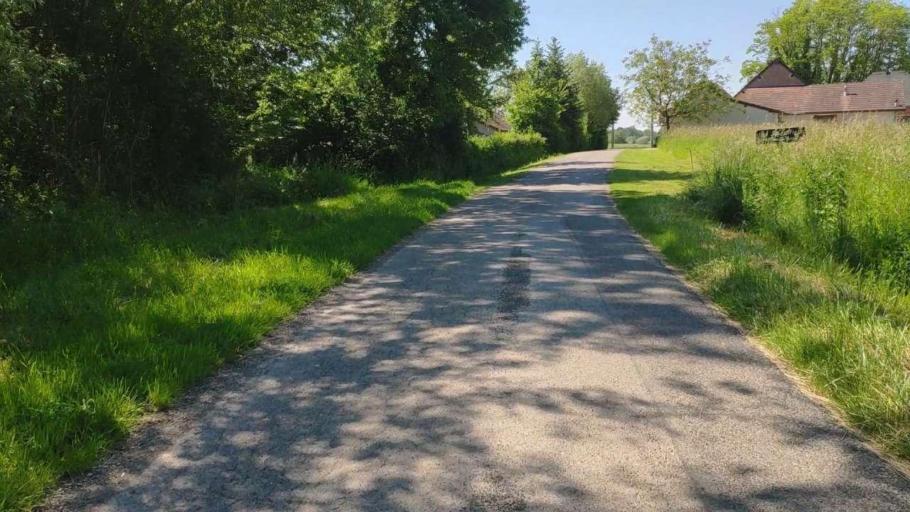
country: FR
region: Franche-Comte
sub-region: Departement du Jura
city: Bletterans
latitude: 46.7827
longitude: 5.4234
